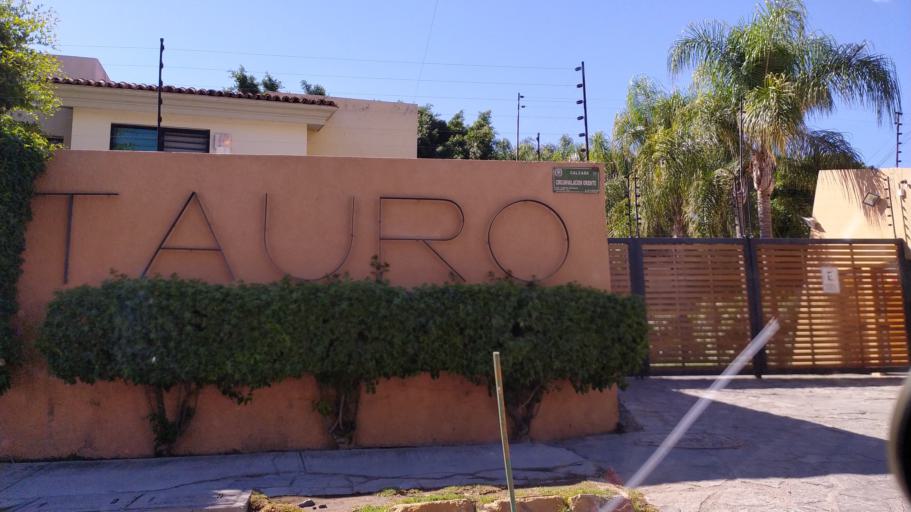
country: MX
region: Jalisco
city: Guadalajara
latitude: 20.6770
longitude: -103.4440
